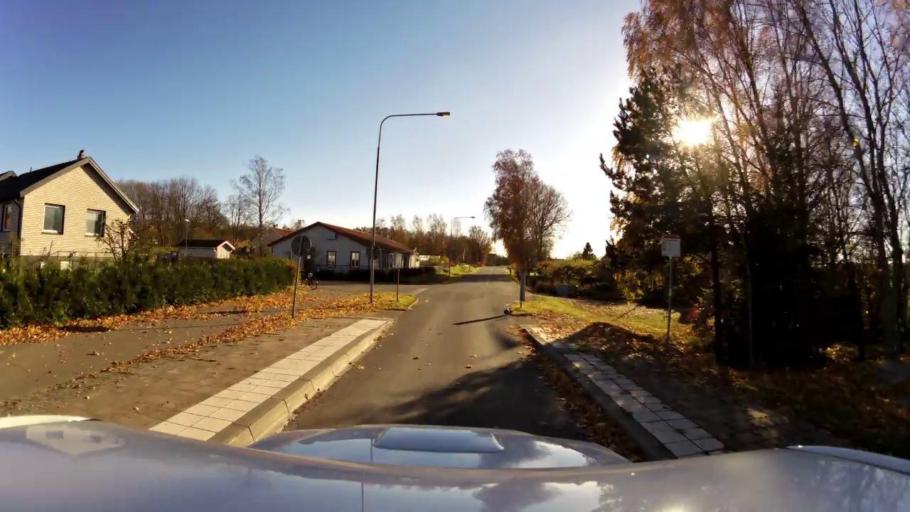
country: SE
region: OEstergoetland
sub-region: Linkopings Kommun
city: Malmslatt
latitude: 58.3616
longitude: 15.5624
